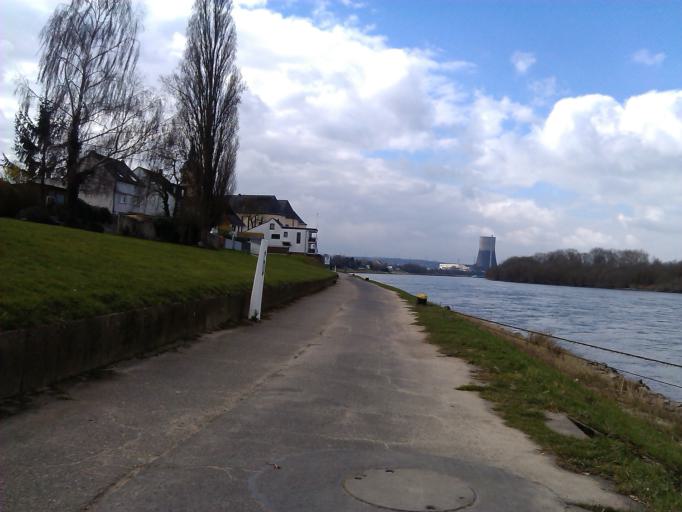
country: DE
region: Rheinland-Pfalz
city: Urmitz
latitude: 50.4180
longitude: 7.5216
